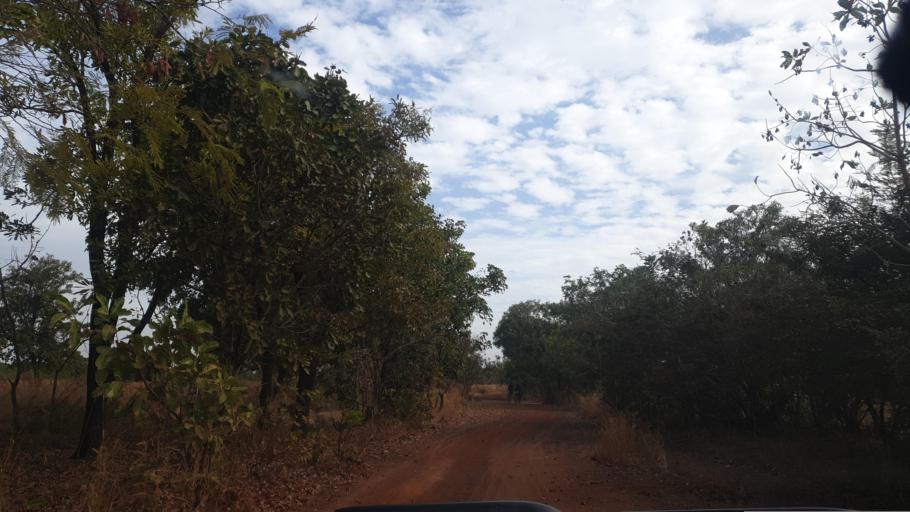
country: ML
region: Sikasso
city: Yanfolila
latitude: 11.3888
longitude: -8.0240
